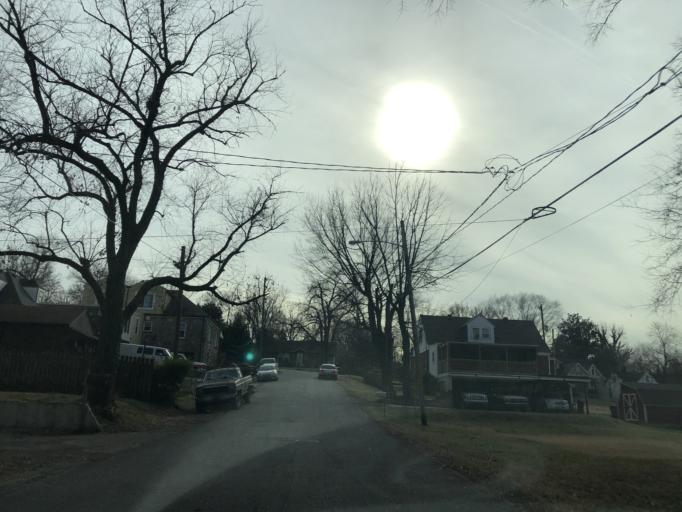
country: US
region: Tennessee
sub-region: Davidson County
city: Nashville
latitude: 36.2147
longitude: -86.7263
